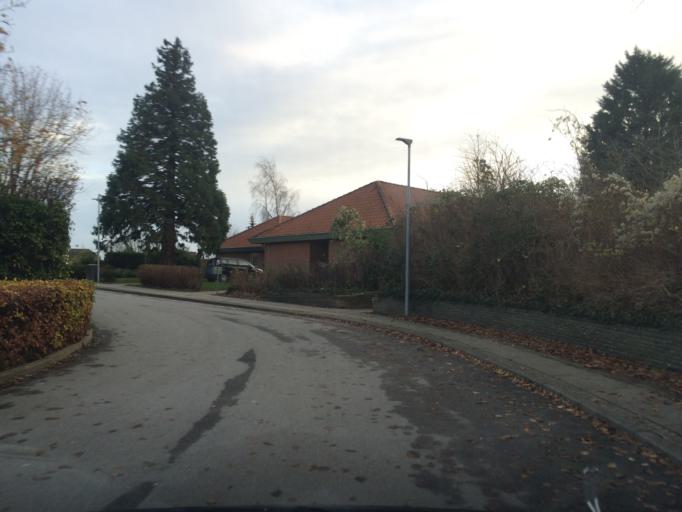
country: DK
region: South Denmark
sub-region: Sonderborg Kommune
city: Augustenborg
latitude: 54.9476
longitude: 9.8730
